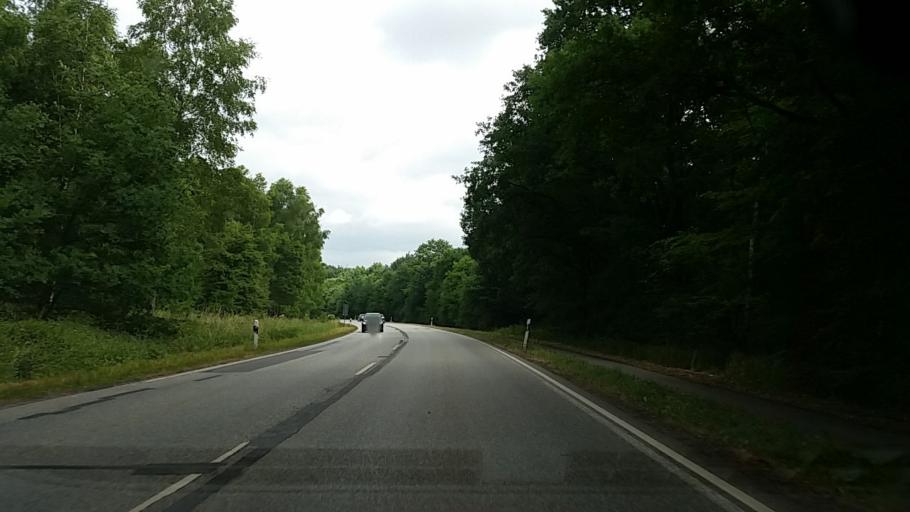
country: DE
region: Schleswig-Holstein
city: Kayhude
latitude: 53.7397
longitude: 10.1191
